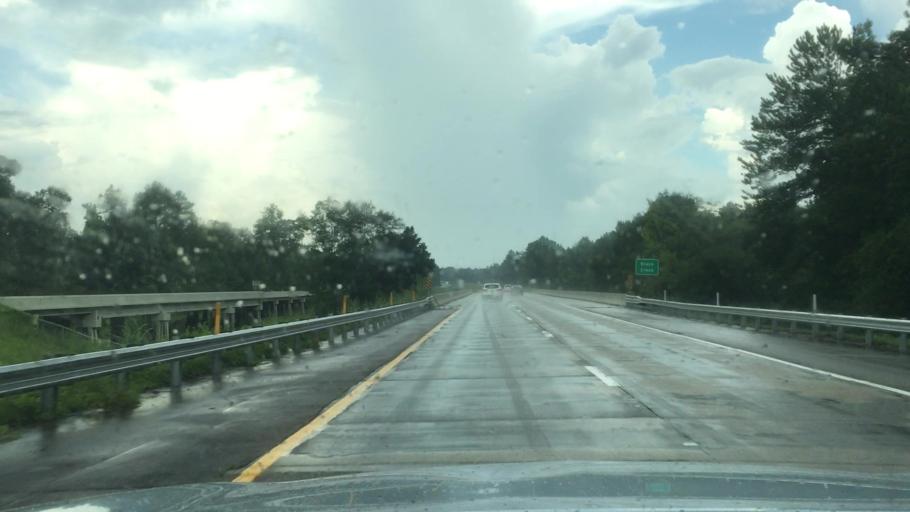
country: US
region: Mississippi
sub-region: Lamar County
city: Purvis
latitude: 31.1680
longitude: -89.3524
